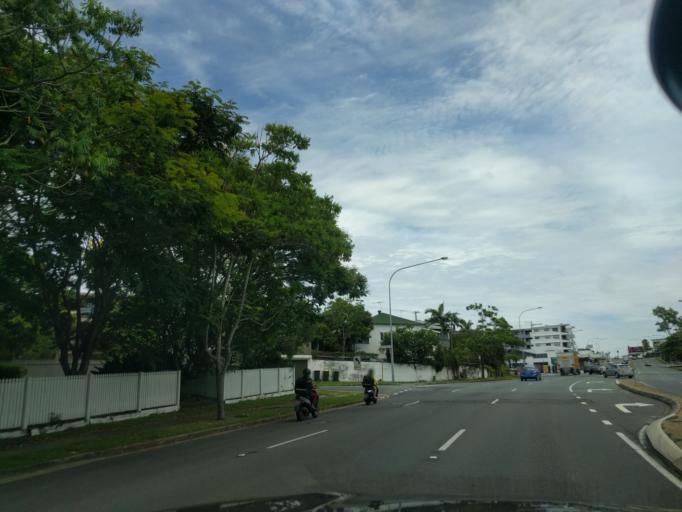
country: AU
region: Queensland
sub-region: Brisbane
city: Grange
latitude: -27.4279
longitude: 153.0029
